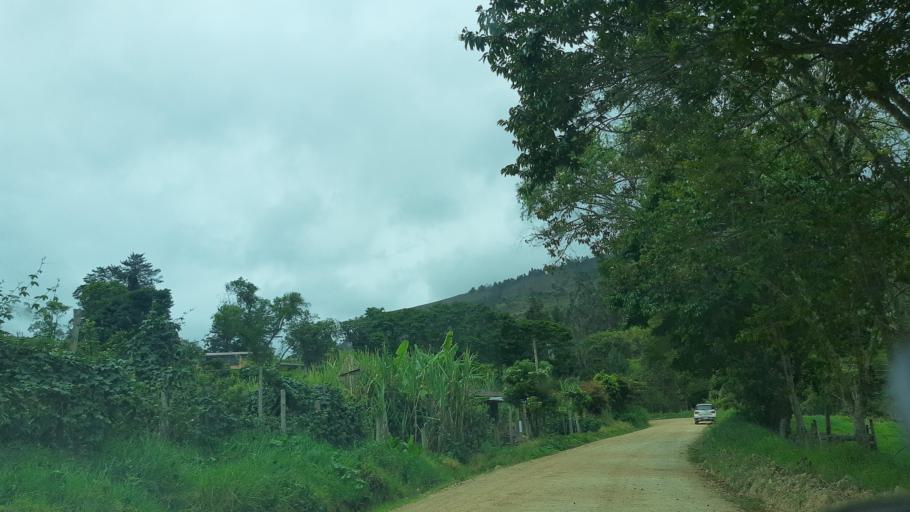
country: CO
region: Boyaca
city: Tibana
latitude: 5.3159
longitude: -73.4374
